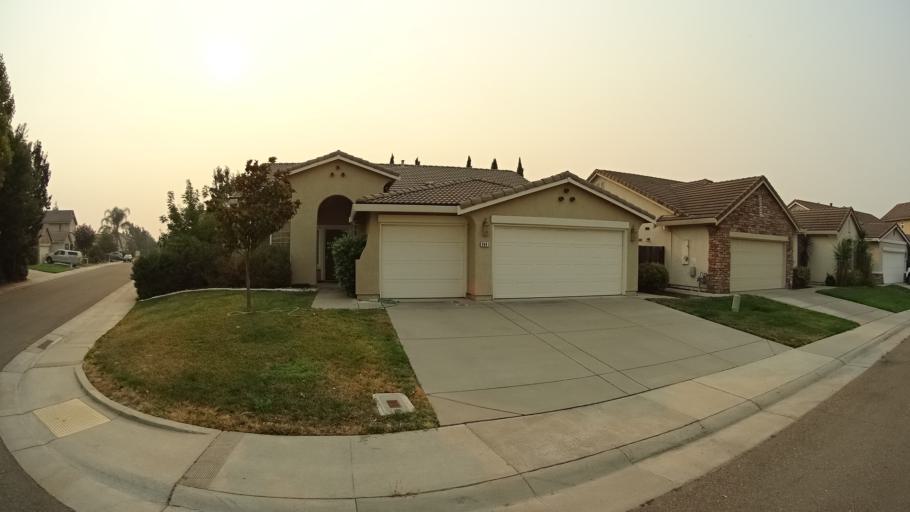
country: US
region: California
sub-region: Sacramento County
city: Laguna
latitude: 38.3957
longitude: -121.4431
